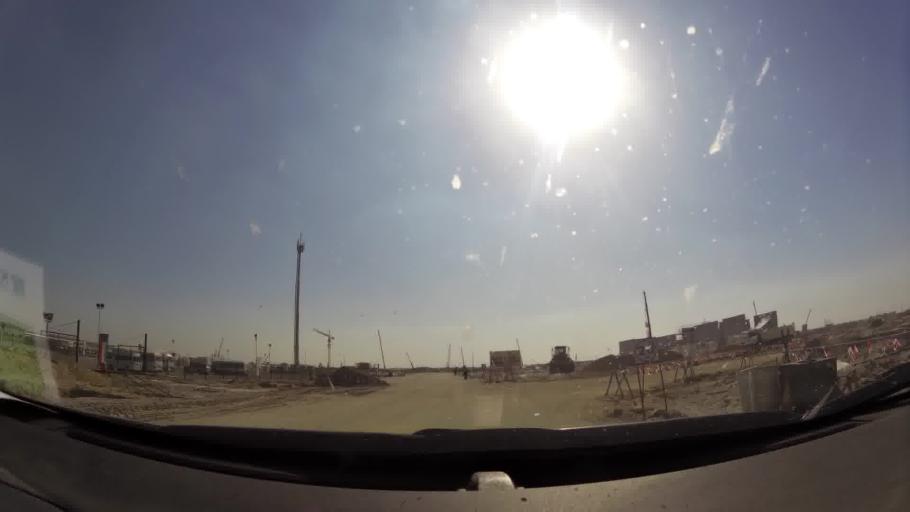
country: SA
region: Eastern Province
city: Al Khafji
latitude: 28.7055
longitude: 48.3404
